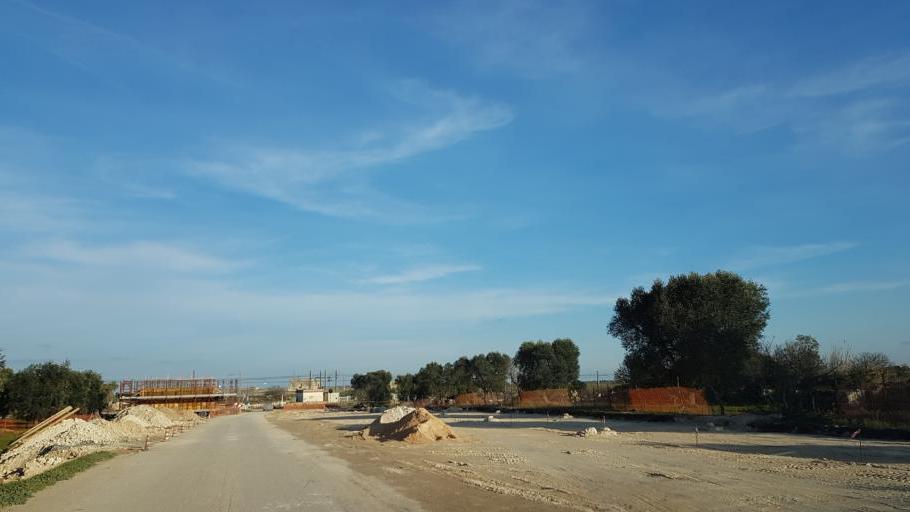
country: IT
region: Apulia
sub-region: Provincia di Brindisi
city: San Vito dei Normanni
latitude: 40.6649
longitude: 17.7894
